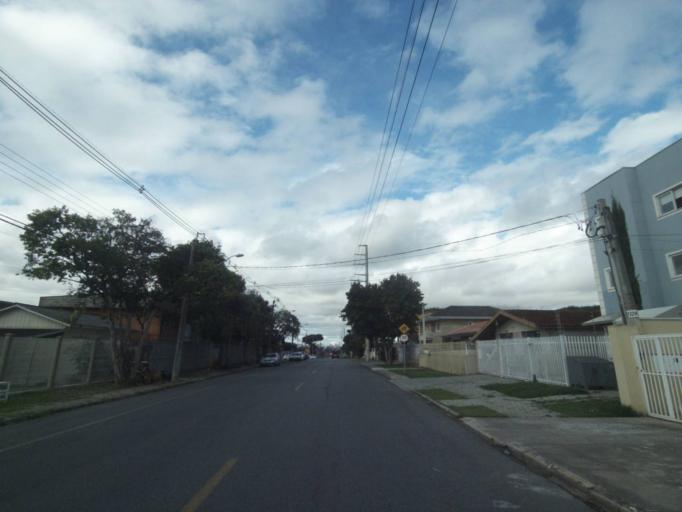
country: BR
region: Parana
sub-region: Curitiba
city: Curitiba
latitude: -25.4805
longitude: -49.2667
